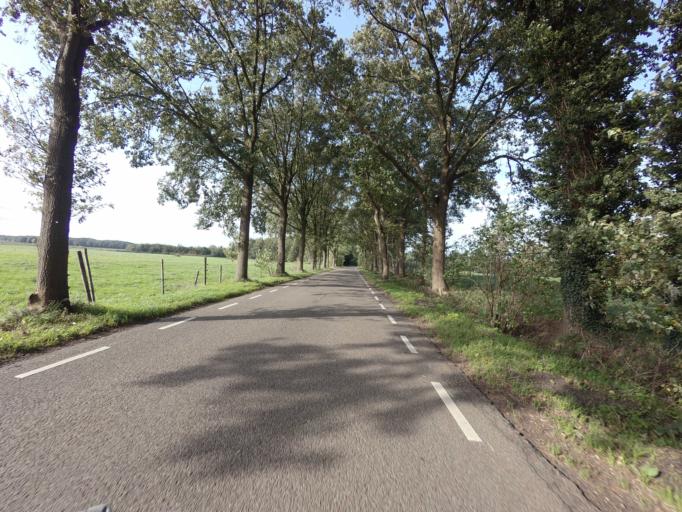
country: NL
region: North Brabant
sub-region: Gemeente Breda
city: Hoge Vucht
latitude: 51.6340
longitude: 4.7929
